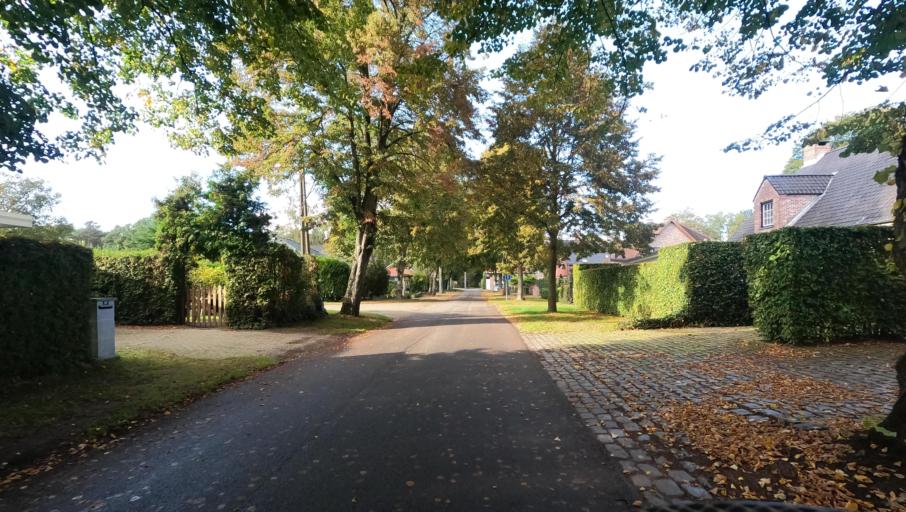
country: BE
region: Flanders
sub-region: Provincie Antwerpen
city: Schilde
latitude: 51.2462
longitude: 4.5879
